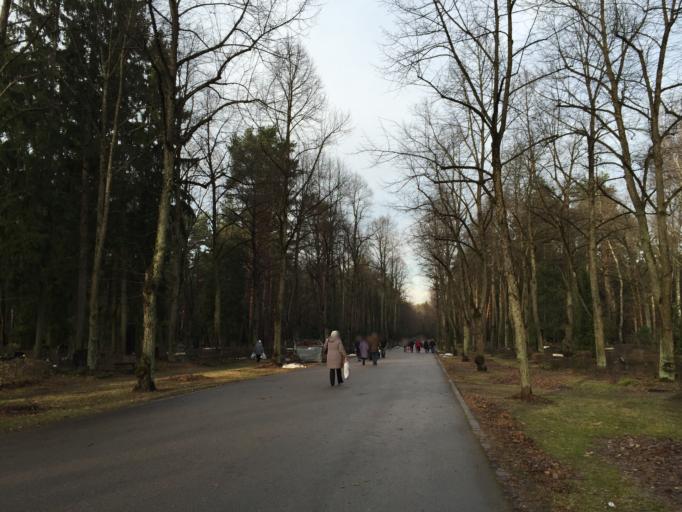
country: LV
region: Riga
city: Jaunciems
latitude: 56.9886
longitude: 24.1464
